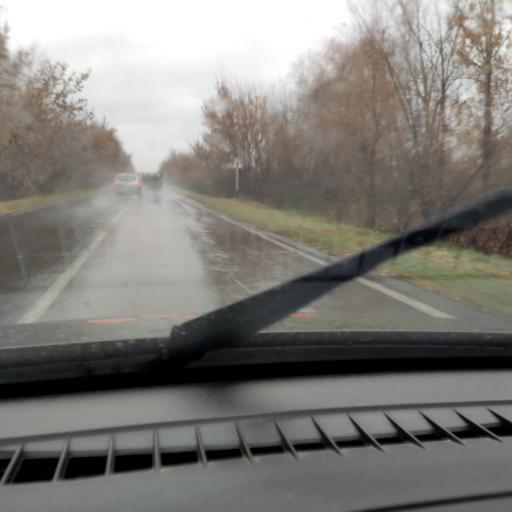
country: RU
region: Samara
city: Tol'yatti
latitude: 53.6897
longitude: 49.2514
